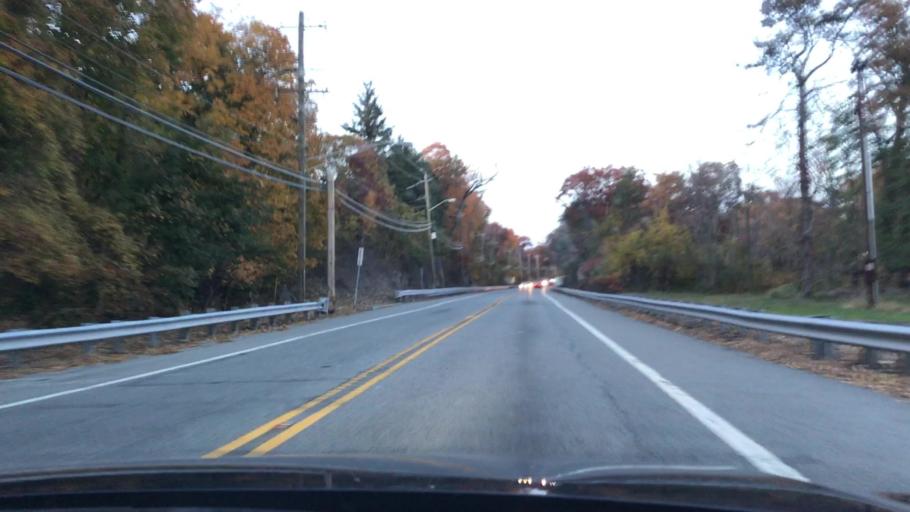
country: US
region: New Jersey
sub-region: Bergen County
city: Alpine
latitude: 40.9483
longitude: -73.9231
